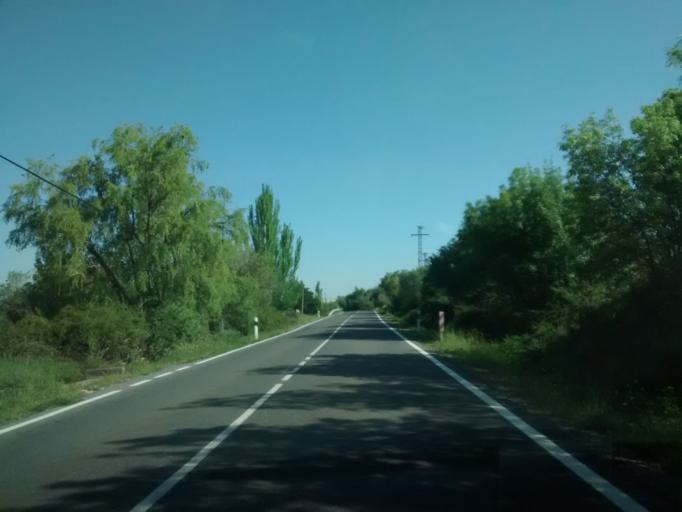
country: ES
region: Castille and Leon
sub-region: Provincia de Segovia
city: Trescasas
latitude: 40.9404
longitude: -4.0334
